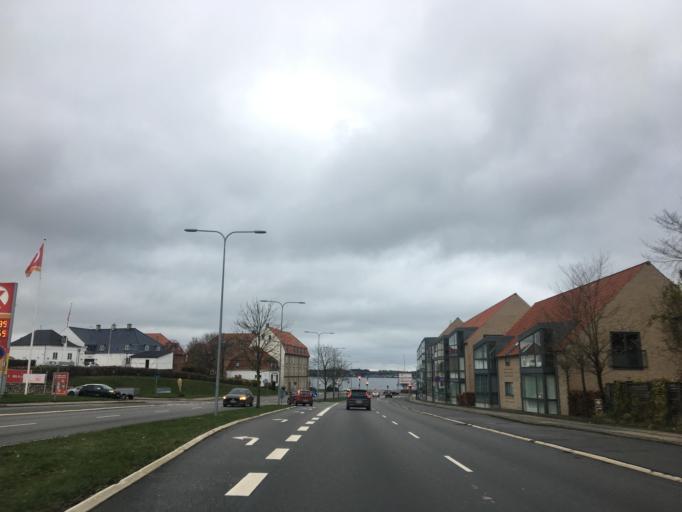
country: DK
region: Zealand
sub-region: Holbaek Kommune
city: Holbaek
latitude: 55.7173
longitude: 11.7064
